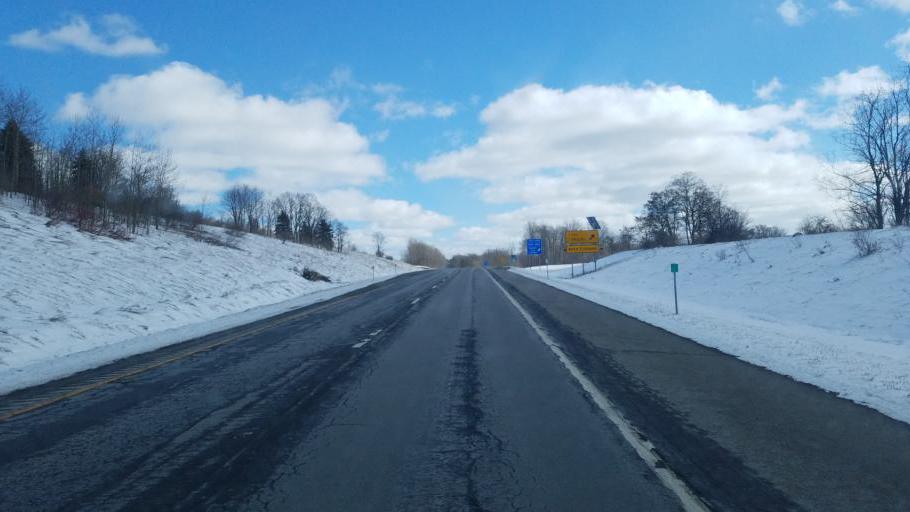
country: US
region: New York
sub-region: Chautauqua County
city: Lakewood
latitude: 42.1432
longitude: -79.3575
